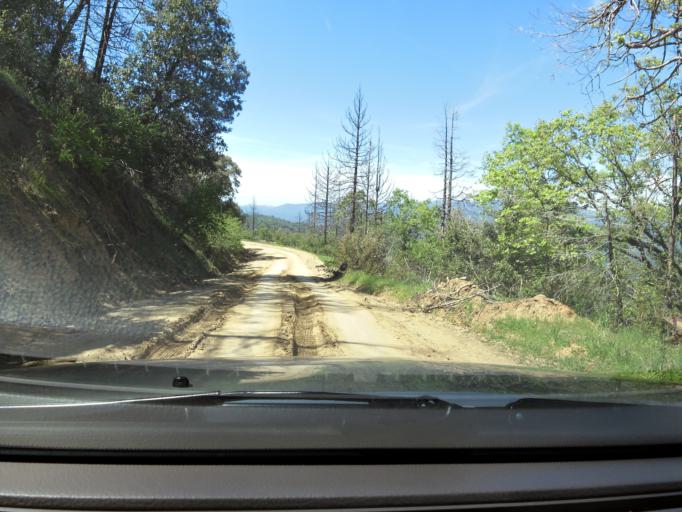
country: US
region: California
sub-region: Madera County
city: Oakhurst
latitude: 37.2847
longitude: -119.6210
